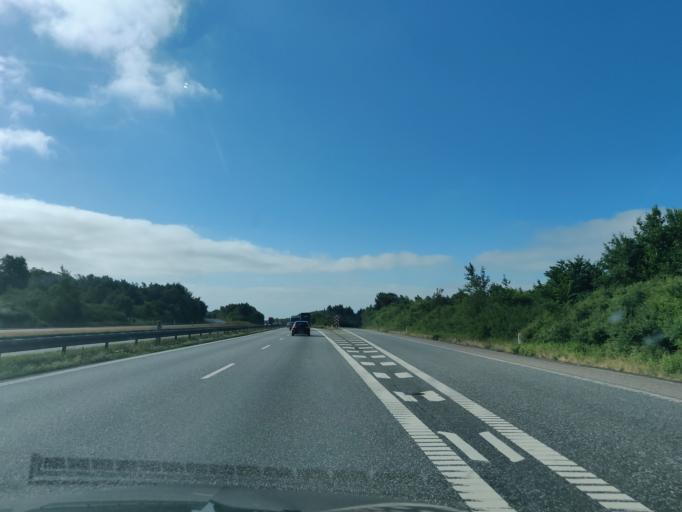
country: DK
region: North Denmark
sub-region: Mariagerfjord Kommune
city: Hobro
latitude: 56.7371
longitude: 9.7020
